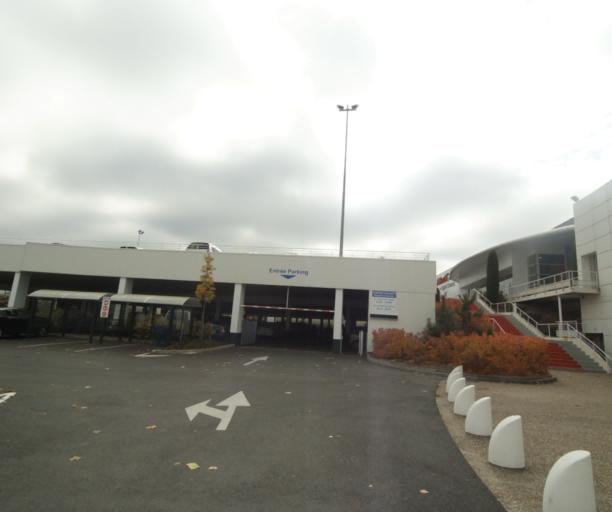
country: FR
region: Poitou-Charentes
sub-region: Departement de la Charente-Maritime
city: Saintes
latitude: 45.7467
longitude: -0.6772
